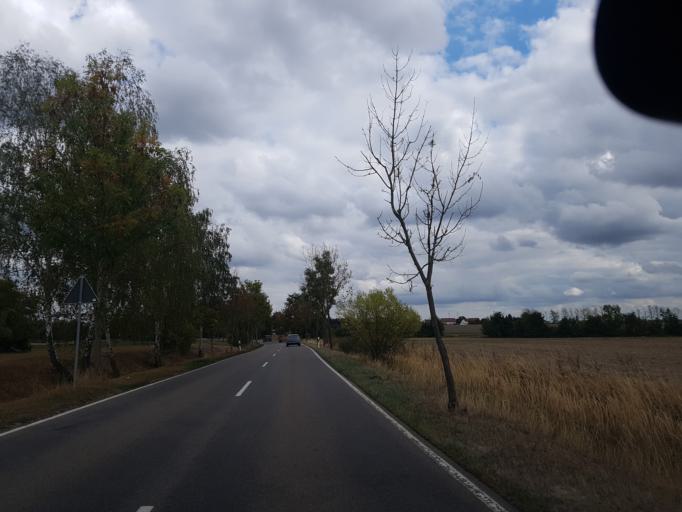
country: DE
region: Saxony-Anhalt
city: Klieken
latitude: 51.9288
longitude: 12.3756
